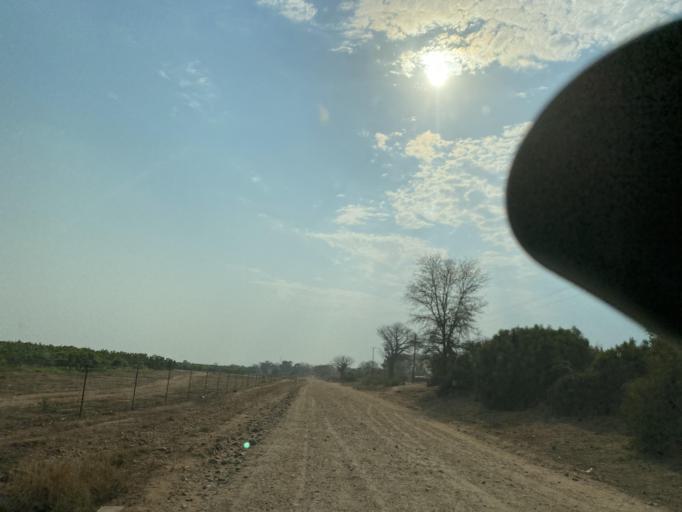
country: ZW
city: Chirundu
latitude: -15.9310
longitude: 28.9568
